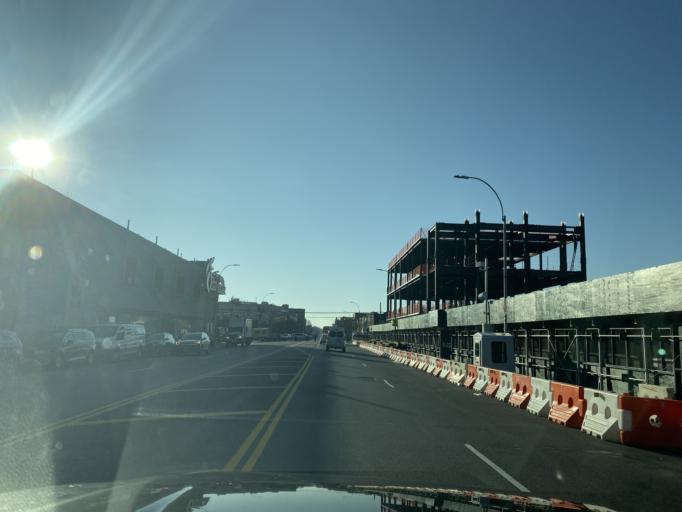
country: US
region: New York
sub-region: Kings County
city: Brooklyn
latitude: 40.6211
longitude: -73.9645
